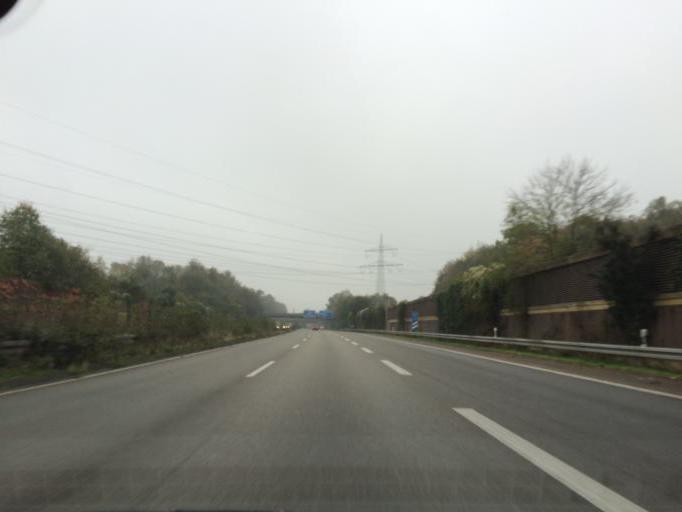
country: DE
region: North Rhine-Westphalia
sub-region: Regierungsbezirk Munster
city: Gladbeck
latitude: 51.5864
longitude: 7.0303
